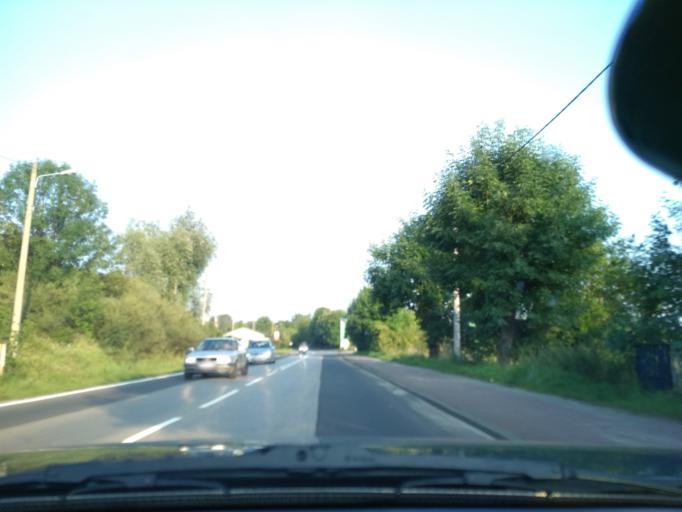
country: PL
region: Silesian Voivodeship
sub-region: Powiat zawiercianski
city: Ogrodzieniec
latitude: 50.4560
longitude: 19.5033
